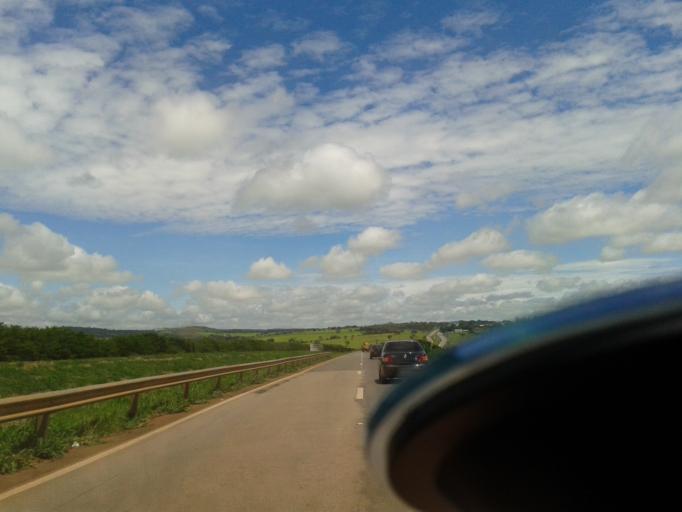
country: BR
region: Goias
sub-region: Inhumas
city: Inhumas
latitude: -16.2858
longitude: -49.5395
